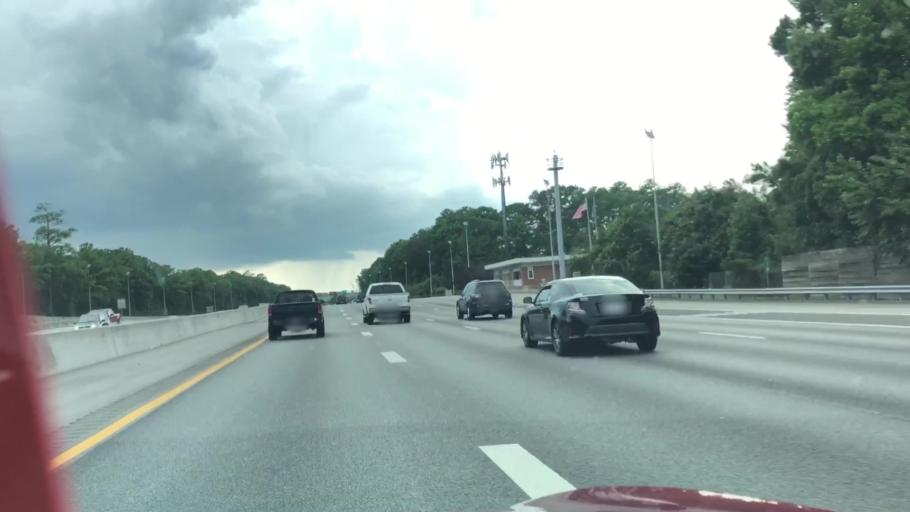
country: US
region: Virginia
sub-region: City of Virginia Beach
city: Virginia Beach
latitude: 36.8342
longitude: -76.1092
